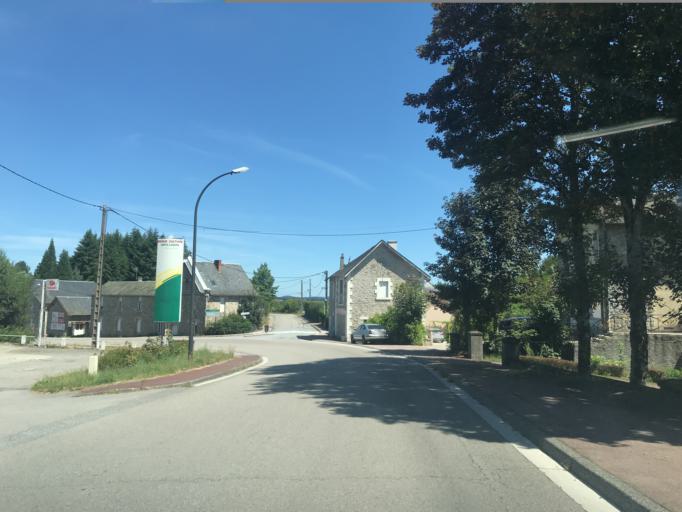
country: FR
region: Limousin
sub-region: Departement de la Correze
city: Egletons
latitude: 45.4073
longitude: 2.0510
